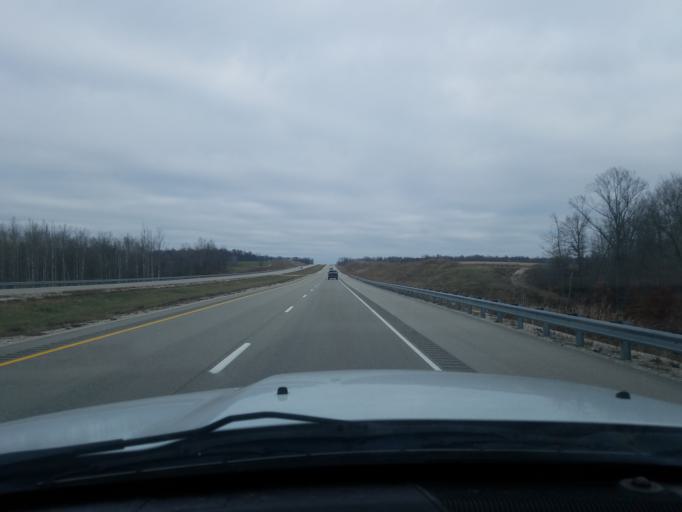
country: US
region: Indiana
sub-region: Greene County
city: Bloomfield
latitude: 38.9325
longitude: -86.8787
